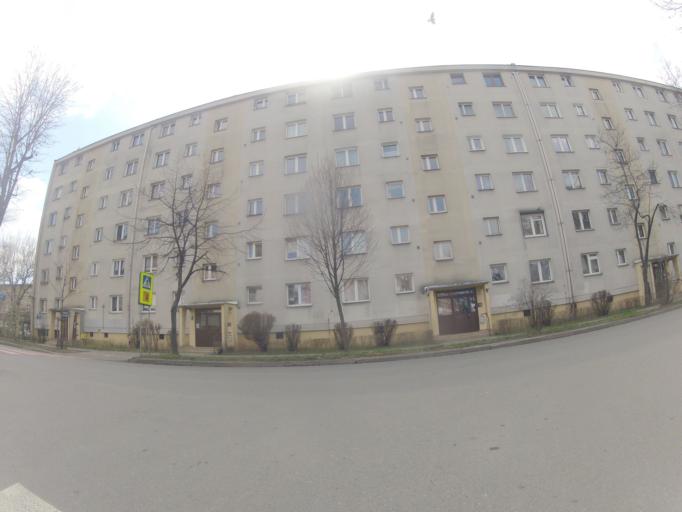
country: PL
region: Lesser Poland Voivodeship
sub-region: Krakow
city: Krakow
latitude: 50.0818
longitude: 19.9548
